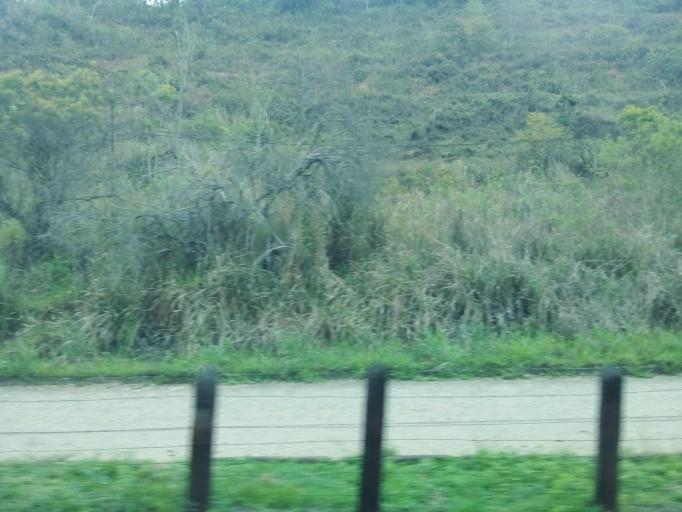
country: BR
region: Minas Gerais
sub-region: Nova Era
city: Nova Era
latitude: -19.7271
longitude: -42.9949
